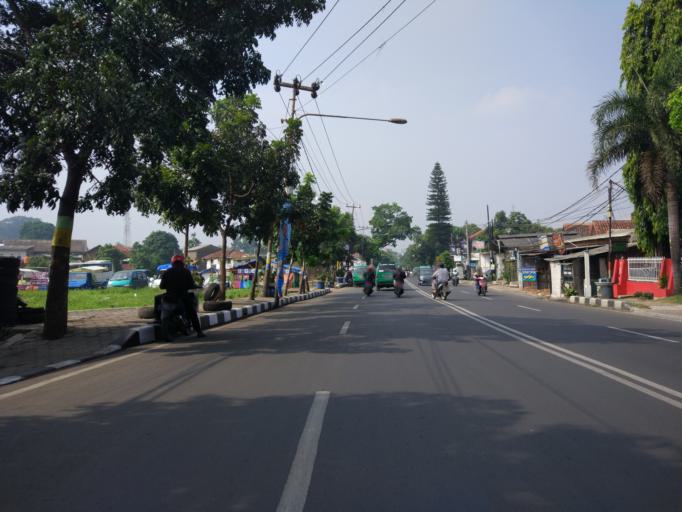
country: ID
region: West Java
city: Cileunyi
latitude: -6.9216
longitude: 107.7097
